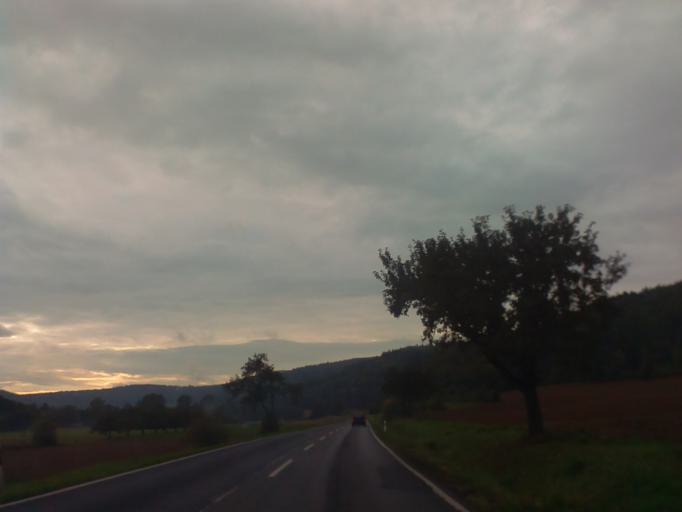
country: DE
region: Bavaria
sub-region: Regierungsbezirk Unterfranken
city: Momlingen
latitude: 49.8473
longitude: 9.0685
